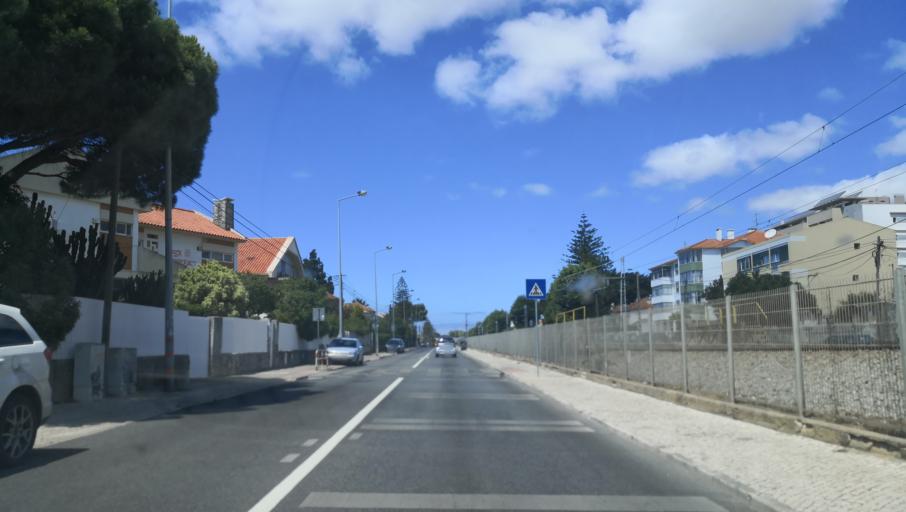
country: PT
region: Lisbon
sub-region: Cascais
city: Parede
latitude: 38.6876
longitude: -9.3416
